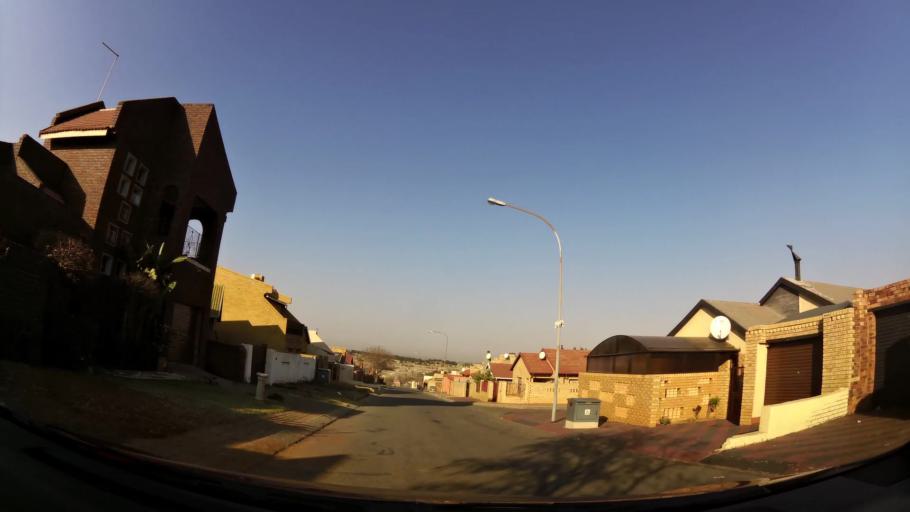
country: ZA
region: Gauteng
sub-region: City of Johannesburg Metropolitan Municipality
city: Soweto
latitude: -26.2523
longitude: 27.9558
